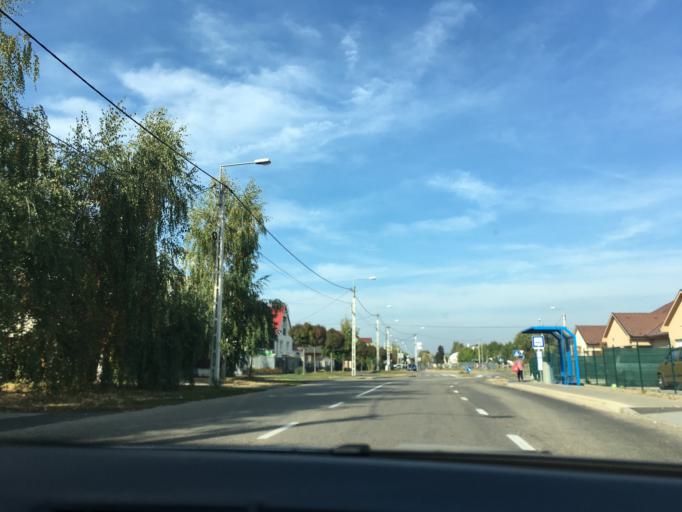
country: HU
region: Hajdu-Bihar
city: Debrecen
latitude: 47.5389
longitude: 21.6713
